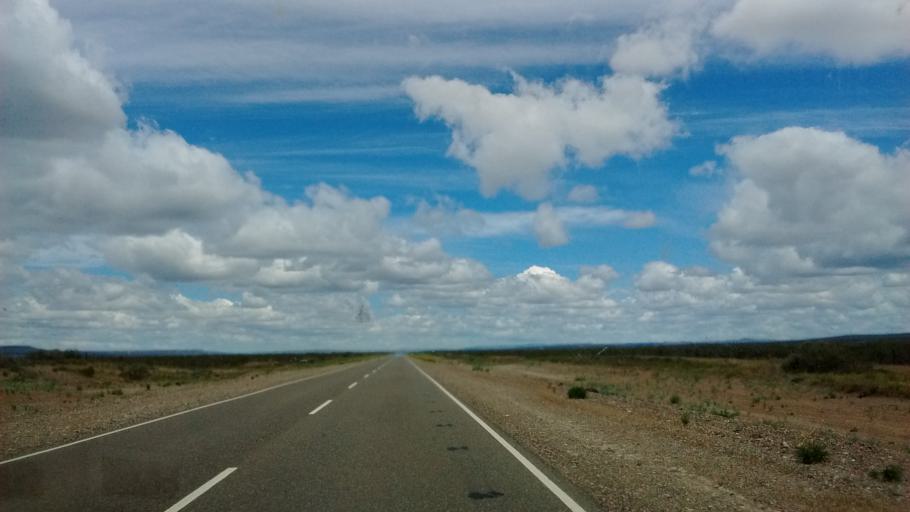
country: AR
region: Neuquen
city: Piedra del Aguila
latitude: -39.8033
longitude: -69.6998
